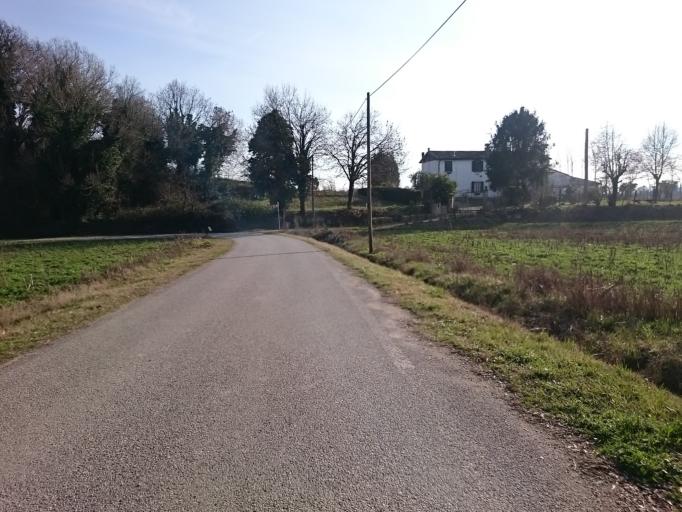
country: IT
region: Veneto
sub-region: Provincia di Verona
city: Salionze
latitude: 45.4151
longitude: 10.7109
